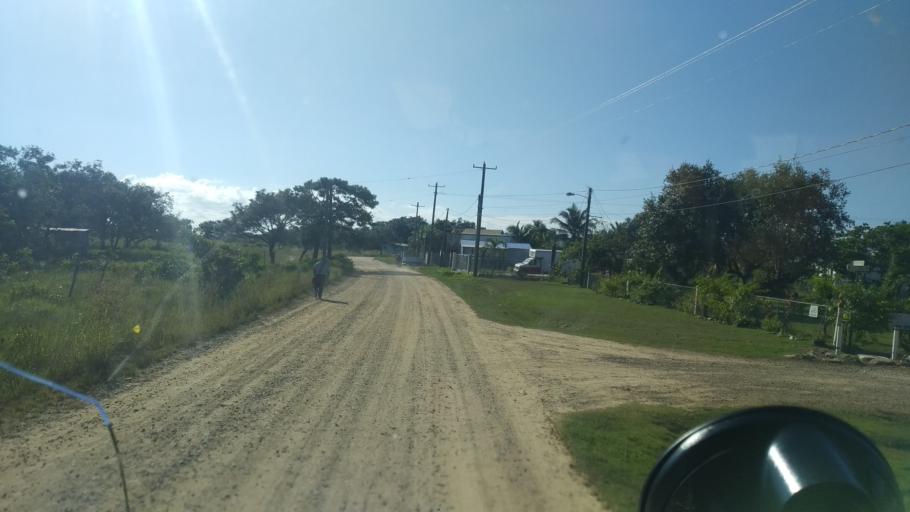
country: BZ
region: Belize
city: Belize City
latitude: 17.5556
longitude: -88.3265
